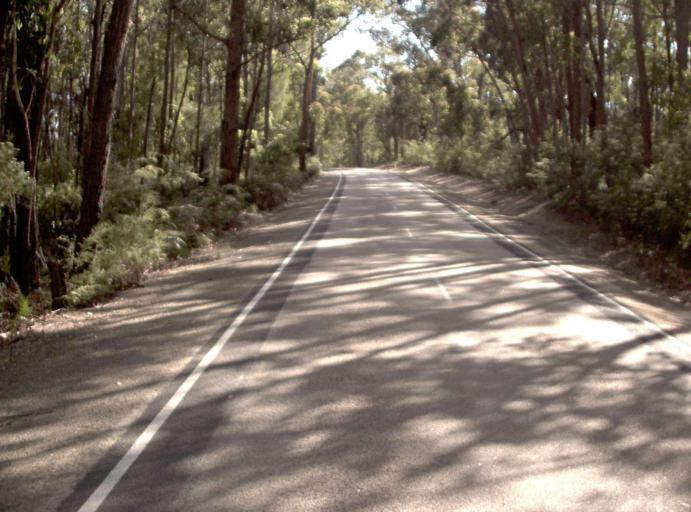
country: AU
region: Victoria
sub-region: East Gippsland
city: Lakes Entrance
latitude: -37.6882
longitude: 148.0466
